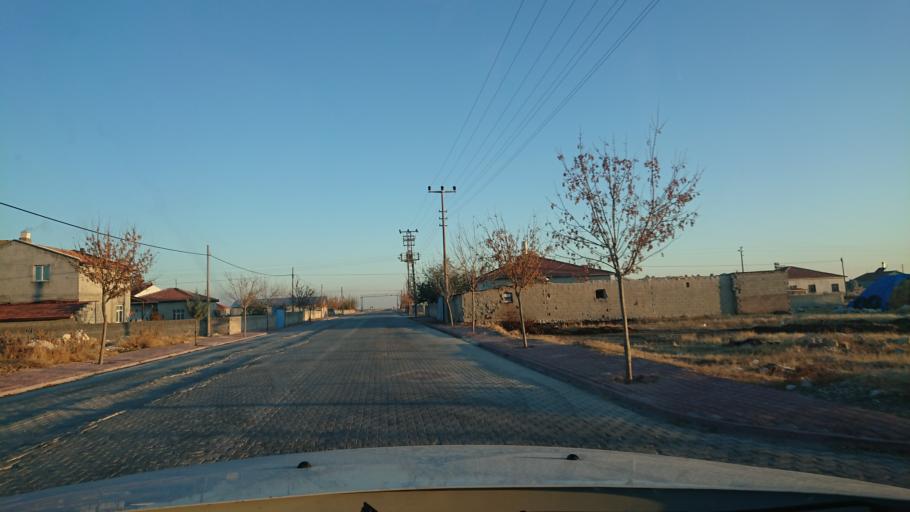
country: TR
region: Aksaray
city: Eskil
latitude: 38.3950
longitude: 33.4246
